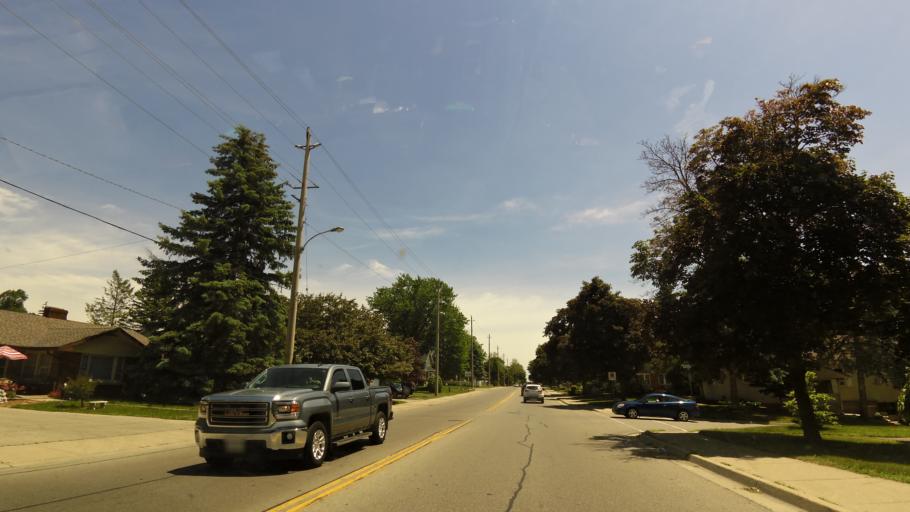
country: CA
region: Ontario
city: Ingersoll
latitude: 42.8691
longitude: -80.7367
